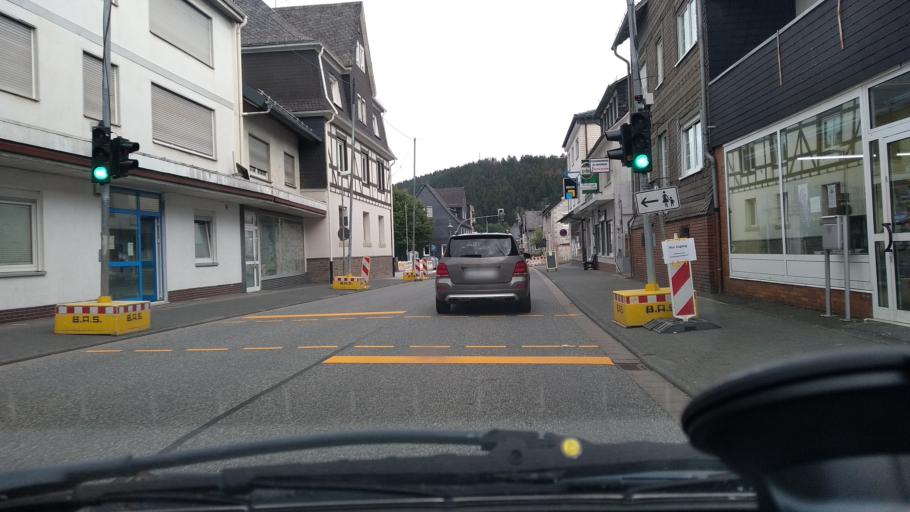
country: DE
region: Hesse
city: Dillenburg
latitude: 50.8332
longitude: 8.3138
